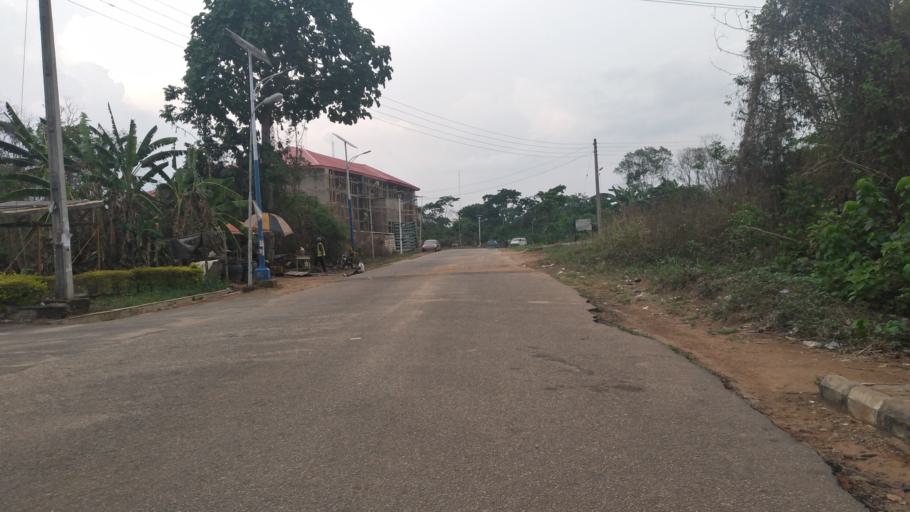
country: NG
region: Ondo
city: Ilare
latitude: 7.2991
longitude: 5.1369
